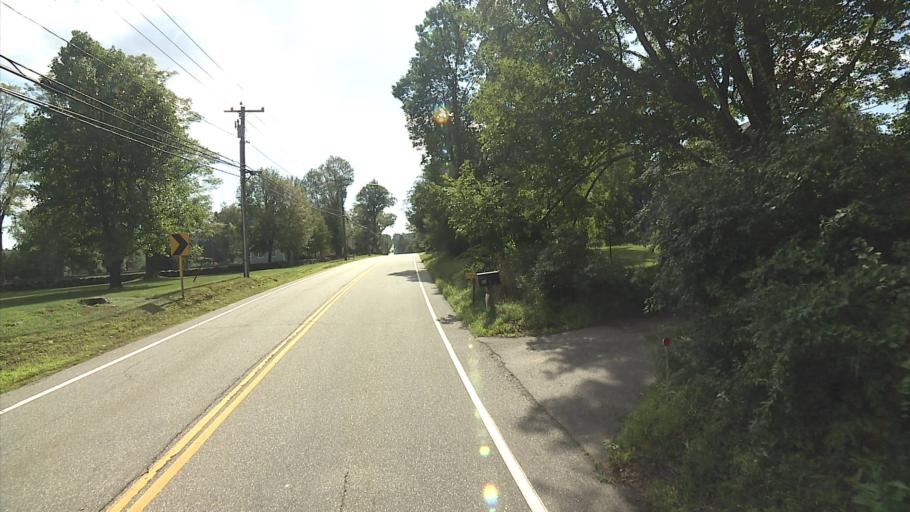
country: US
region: Connecticut
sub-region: Tolland County
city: Stafford Springs
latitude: 41.9577
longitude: -72.2860
